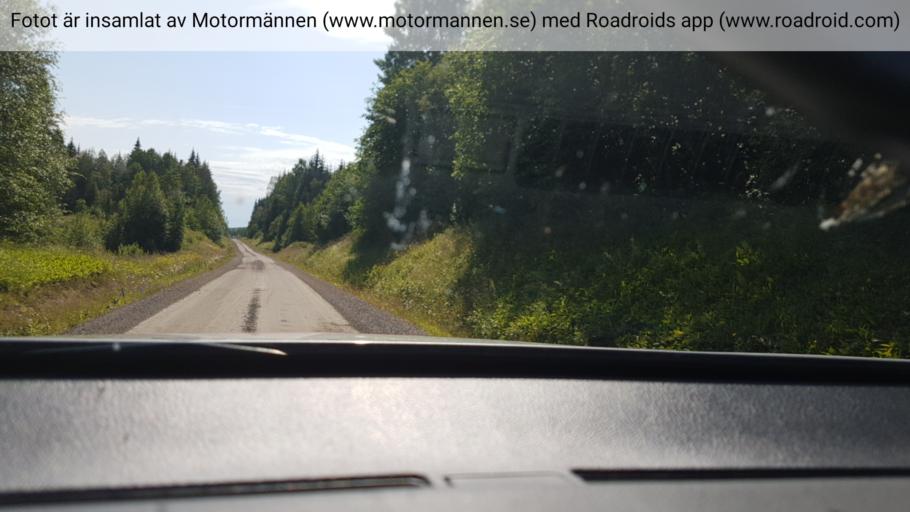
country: SE
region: Vaermland
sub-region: Torsby Kommun
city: Torsby
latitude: 60.5360
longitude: 13.1110
